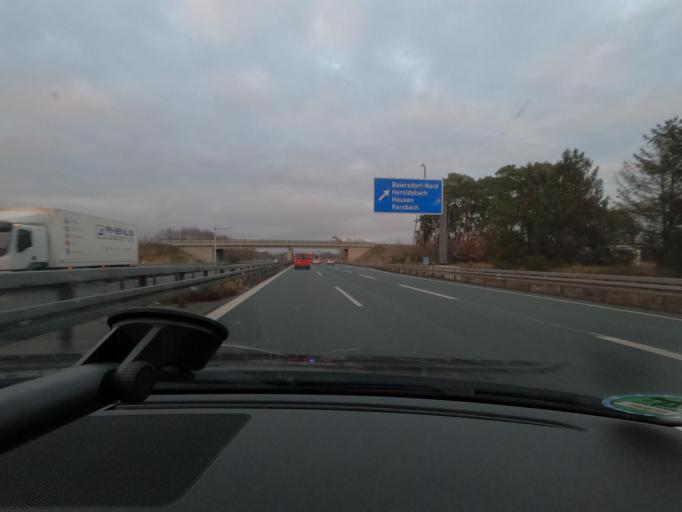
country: DE
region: Bavaria
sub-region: Regierungsbezirk Mittelfranken
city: Baiersdorf
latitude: 49.6746
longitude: 11.0487
